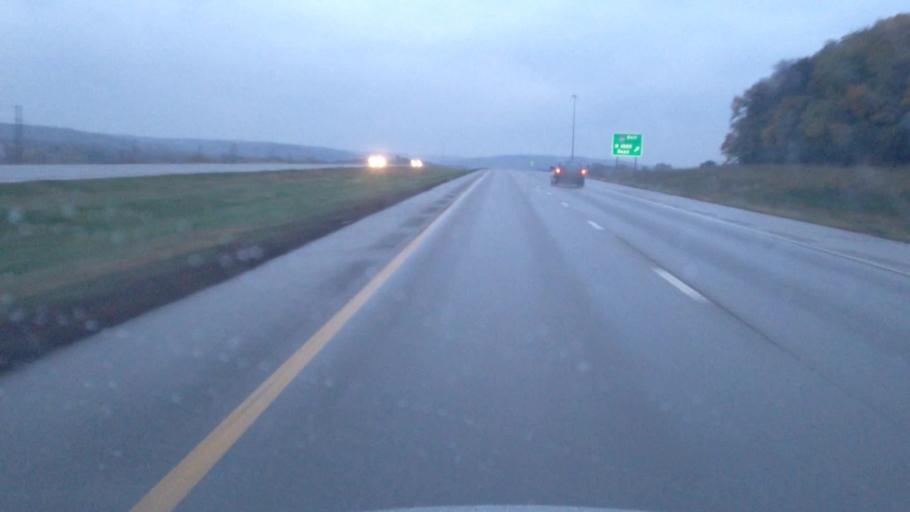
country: US
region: Kansas
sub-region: Douglas County
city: Lawrence
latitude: 38.8900
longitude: -95.2600
